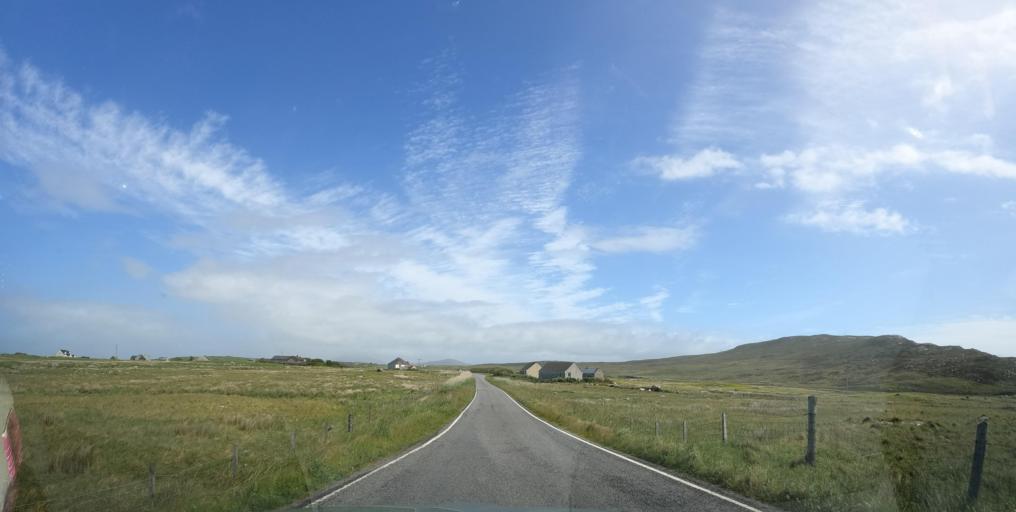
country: GB
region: Scotland
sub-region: Eilean Siar
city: Isle of South Uist
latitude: 57.1131
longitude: -7.3677
